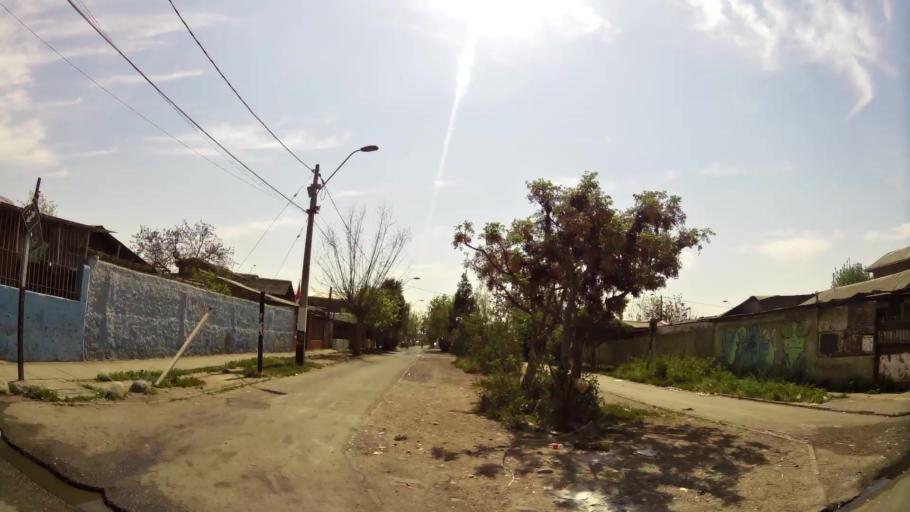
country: CL
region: Santiago Metropolitan
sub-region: Provincia de Santiago
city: La Pintana
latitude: -33.5482
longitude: -70.6410
